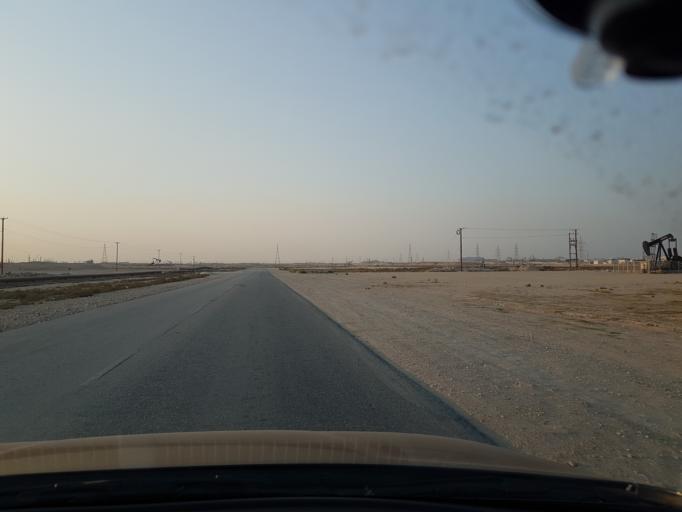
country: BH
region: Central Governorate
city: Dar Kulayb
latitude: 26.0087
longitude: 50.5809
